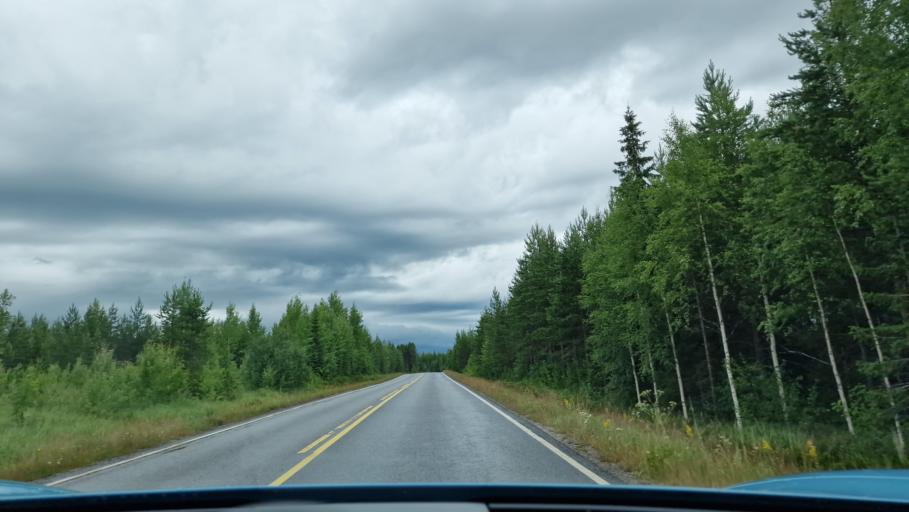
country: FI
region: Southern Ostrobothnia
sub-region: Jaerviseutu
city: Soini
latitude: 62.7133
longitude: 24.4399
